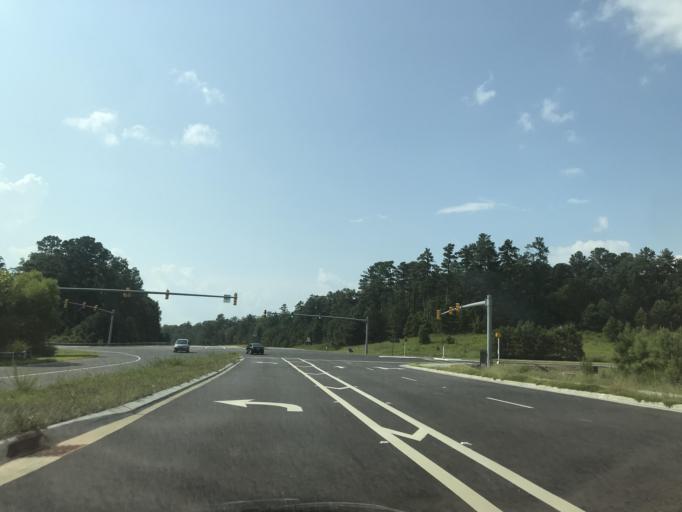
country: US
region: North Carolina
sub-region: Wake County
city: Morrisville
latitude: 35.8468
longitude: -78.8796
